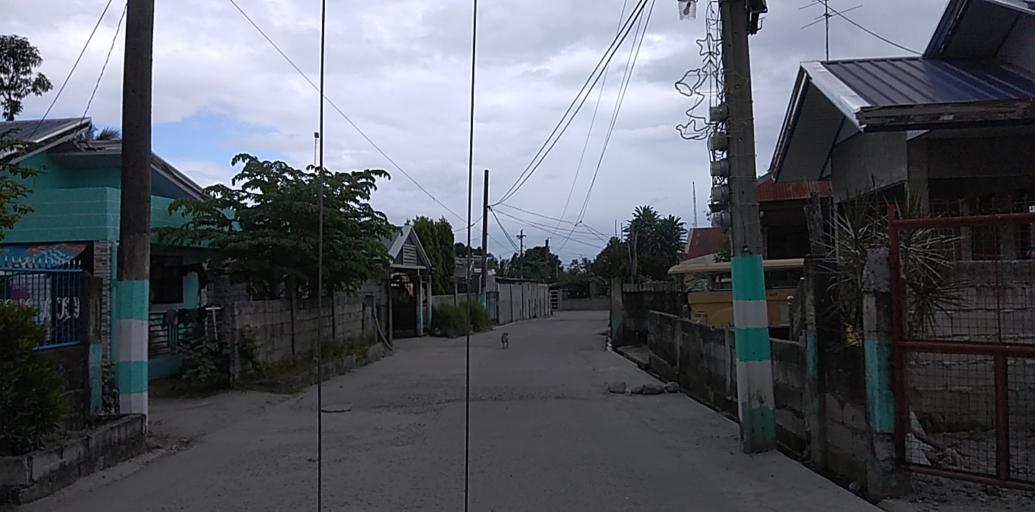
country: PH
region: Central Luzon
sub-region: Province of Pampanga
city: Pio
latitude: 15.0445
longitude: 120.5368
